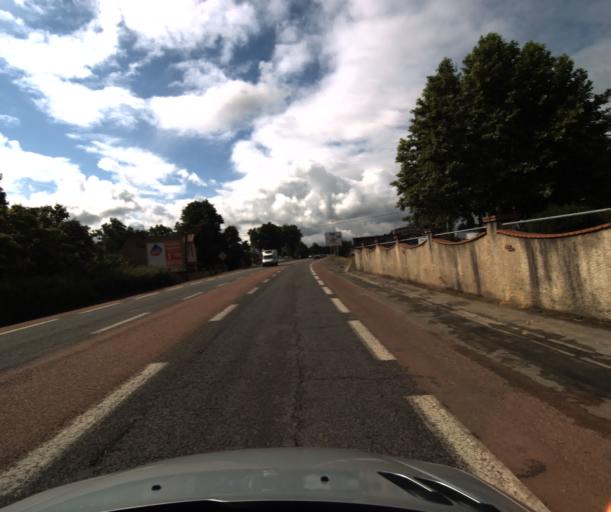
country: FR
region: Midi-Pyrenees
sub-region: Departement du Tarn-et-Garonne
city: Castelsarrasin
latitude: 44.0601
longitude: 1.0984
